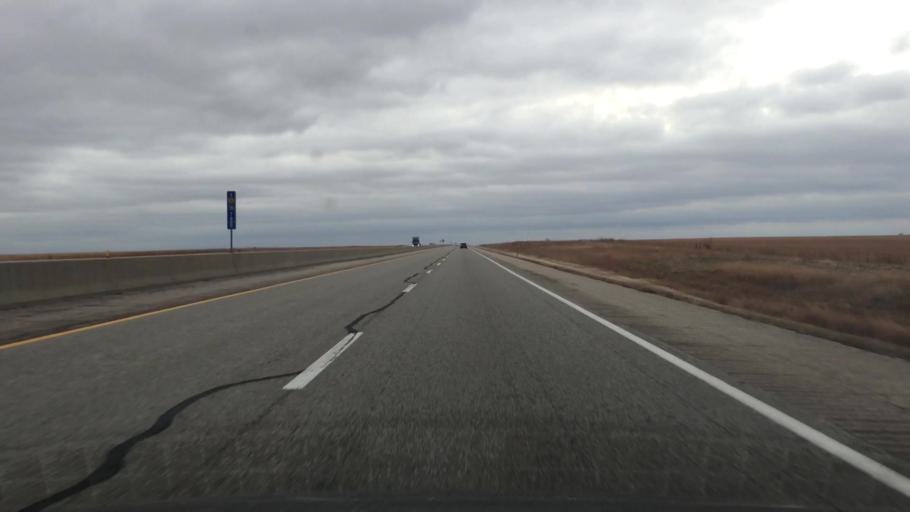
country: US
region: Kansas
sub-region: Butler County
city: El Dorado
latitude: 37.9103
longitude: -96.8119
